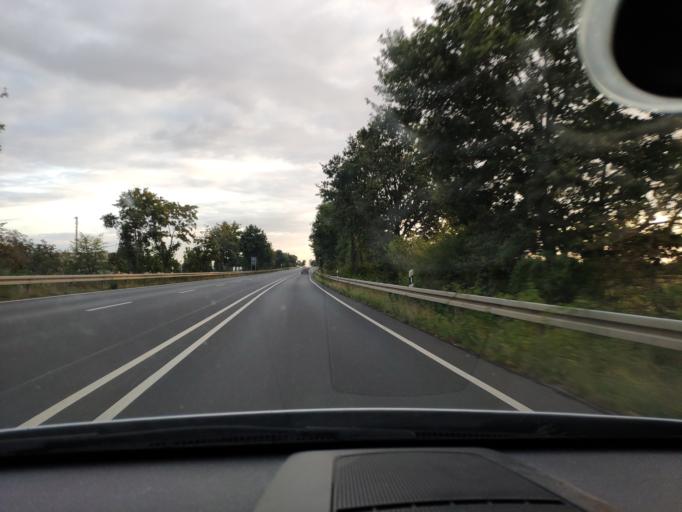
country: DE
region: North Rhine-Westphalia
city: Geilenkirchen
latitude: 50.9770
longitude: 6.0943
